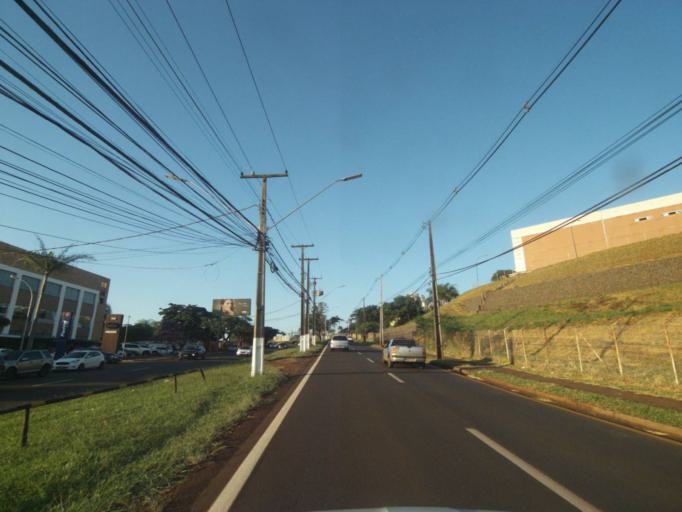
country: BR
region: Parana
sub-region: Londrina
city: Londrina
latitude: -23.3432
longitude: -51.1884
